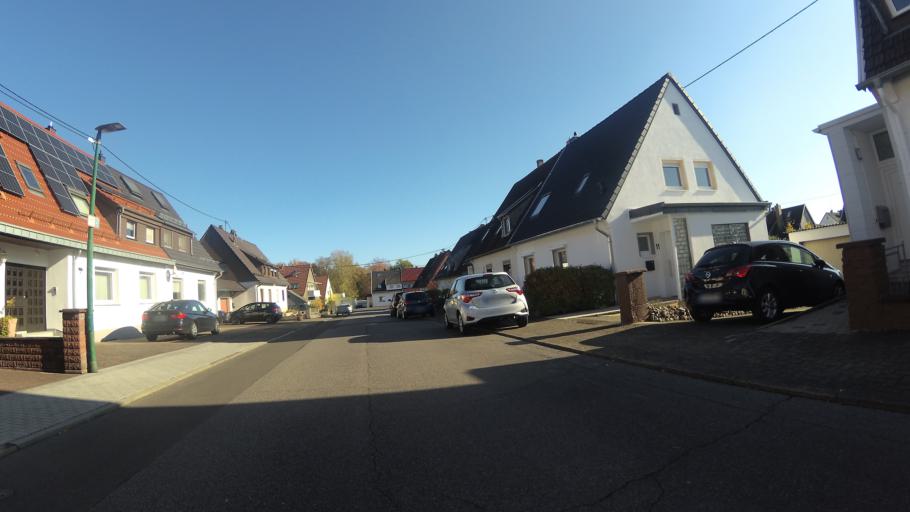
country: DE
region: Saarland
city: Neunkirchen
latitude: 49.3438
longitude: 7.1996
